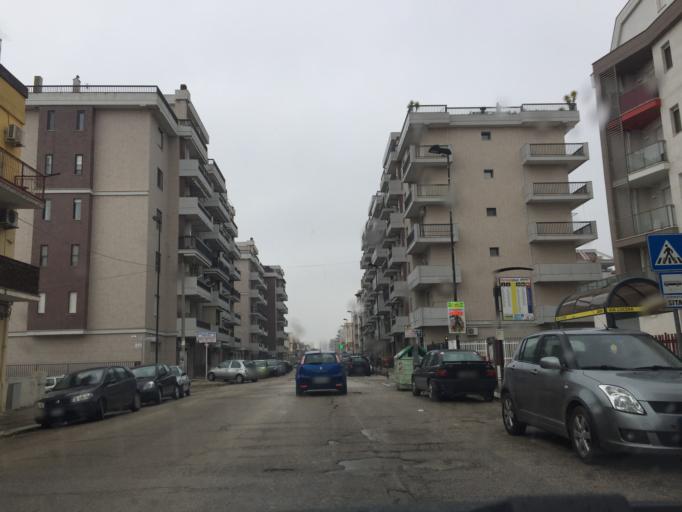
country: IT
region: Apulia
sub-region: Provincia di Foggia
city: Foggia
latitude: 41.4669
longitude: 15.5305
